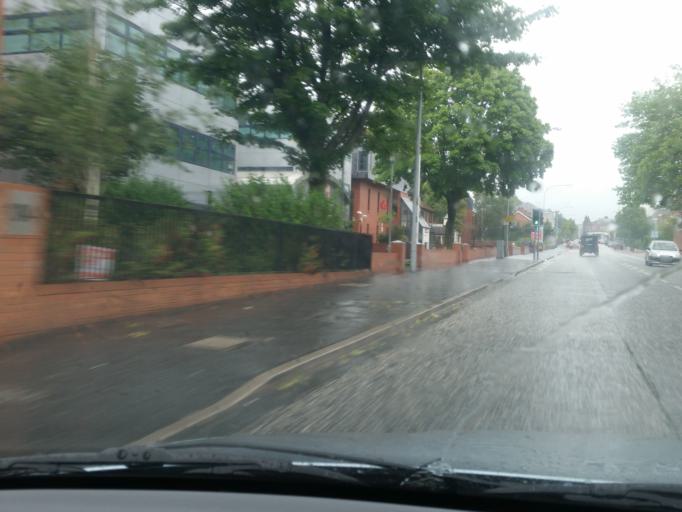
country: GB
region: Northern Ireland
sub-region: Castlereagh District
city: Castlereagh
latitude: 54.5992
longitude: -5.8839
